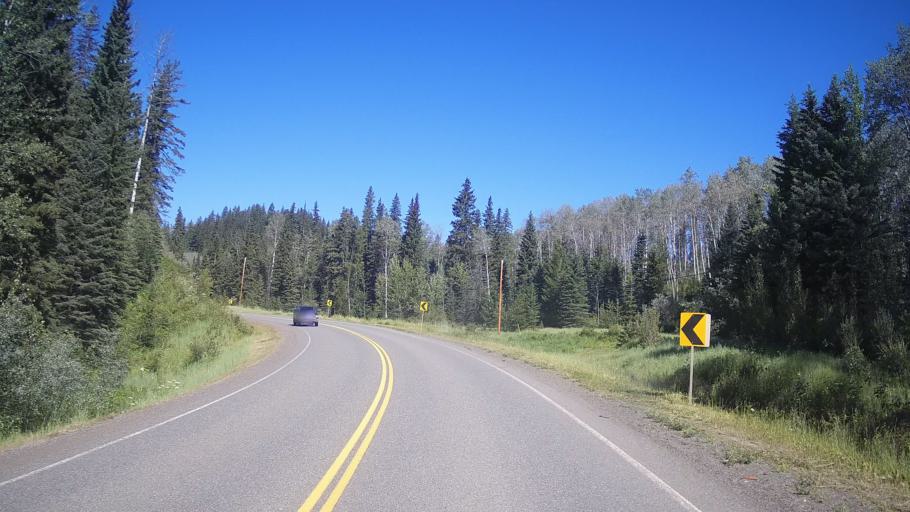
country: CA
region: British Columbia
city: Kamloops
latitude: 51.5047
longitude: -120.6021
